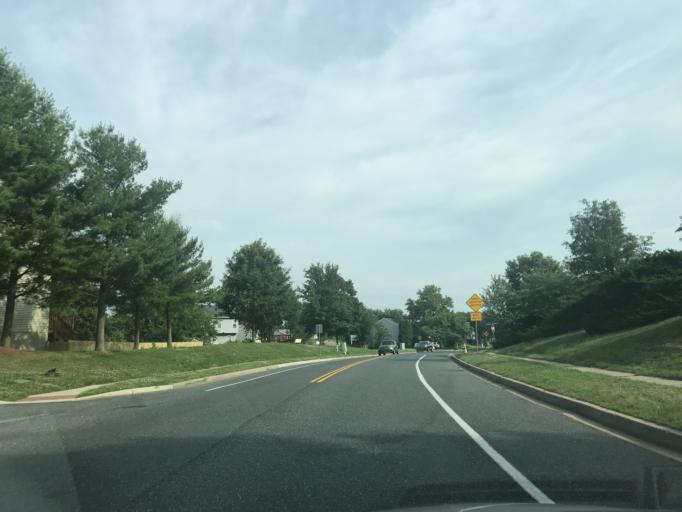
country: US
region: Maryland
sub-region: Harford County
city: Edgewood
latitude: 39.4265
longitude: -76.3226
